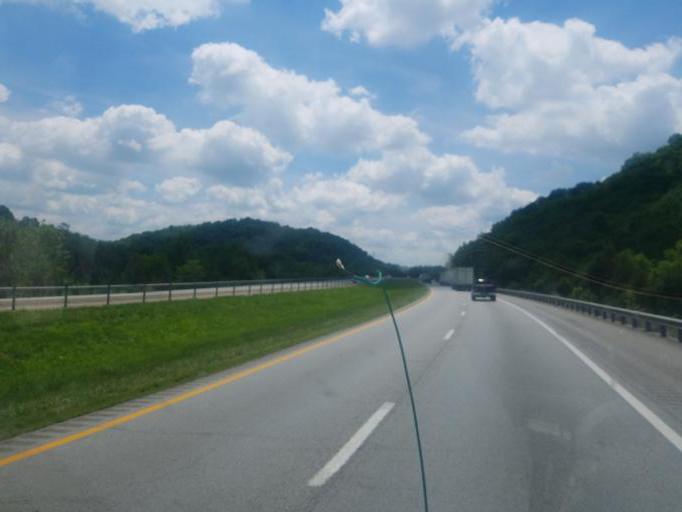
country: US
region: Kentucky
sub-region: Trimble County
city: Providence
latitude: 38.6097
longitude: -85.1681
